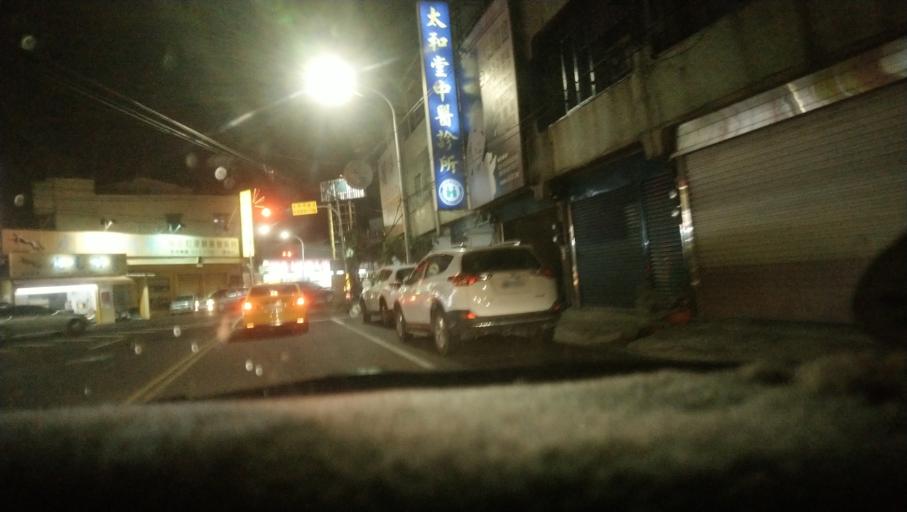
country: TW
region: Taiwan
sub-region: Yunlin
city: Douliu
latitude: 23.7007
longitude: 120.4255
